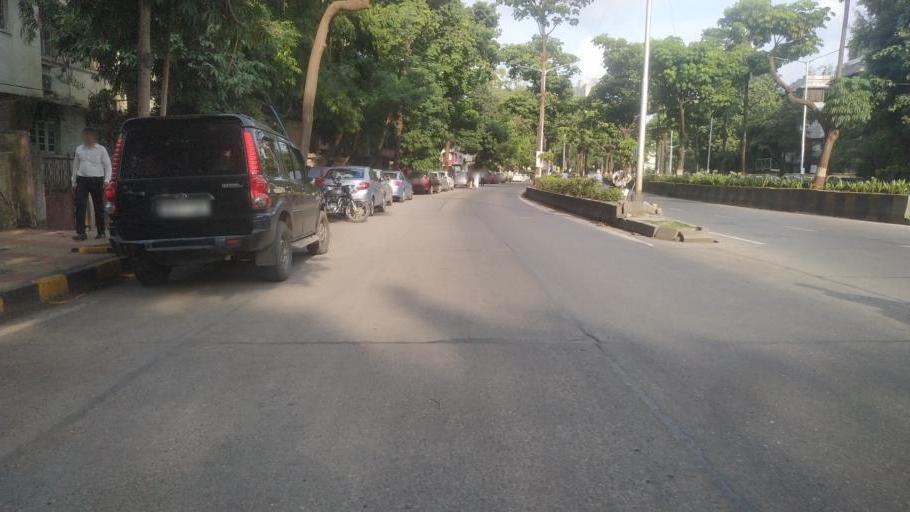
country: IN
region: Maharashtra
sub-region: Mumbai Suburban
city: Mumbai
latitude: 19.0290
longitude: 72.8582
